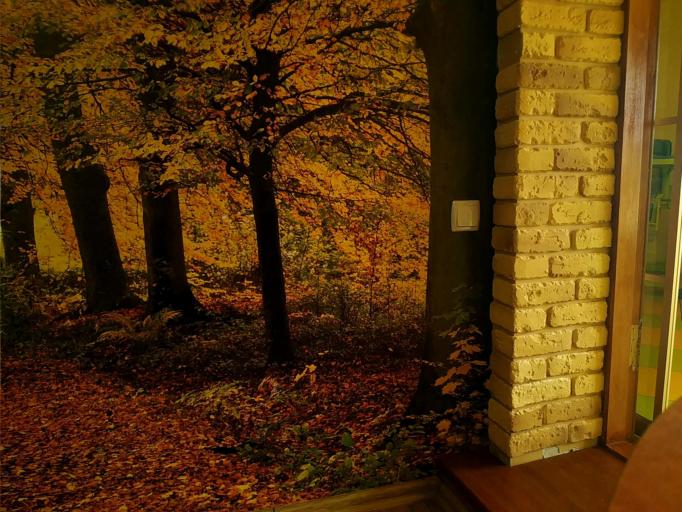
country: RU
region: Smolensk
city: Safonovo
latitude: 55.1070
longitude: 33.1407
